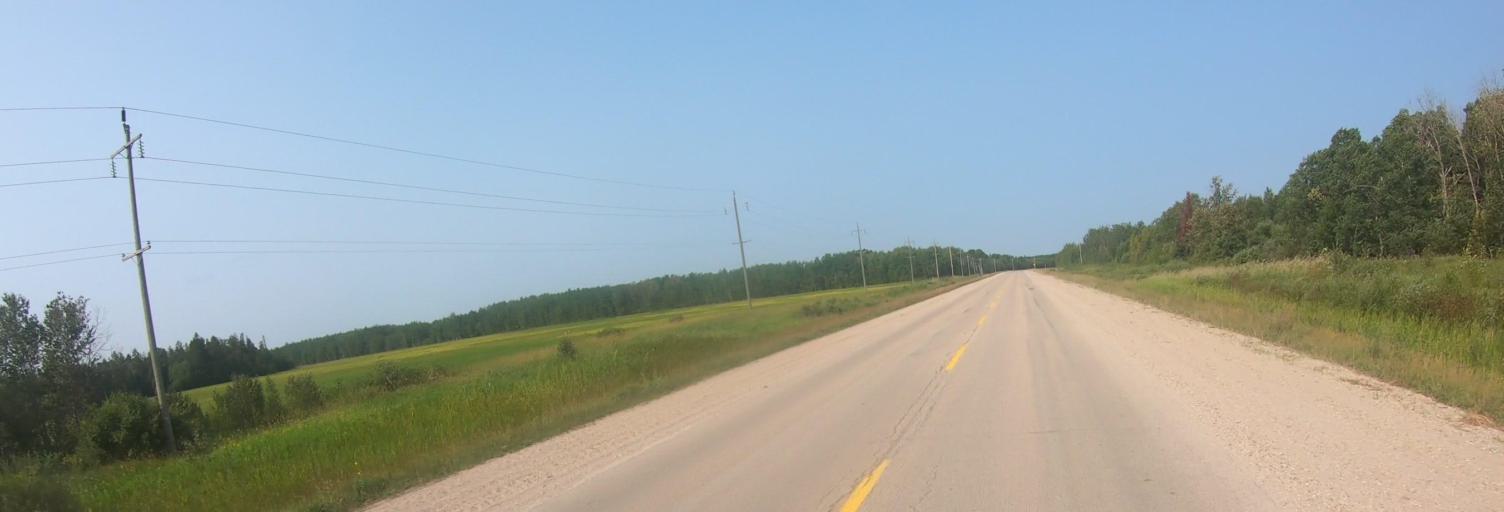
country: US
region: Minnesota
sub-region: Roseau County
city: Roseau
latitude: 49.0234
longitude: -95.7275
